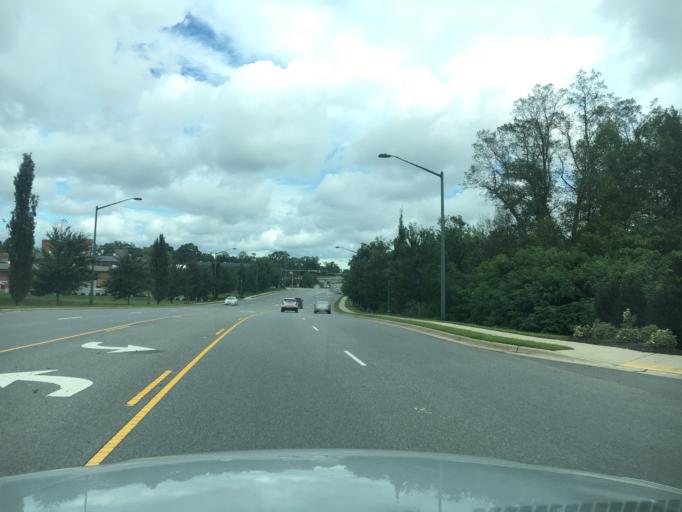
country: US
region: North Carolina
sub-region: Catawba County
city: Hickory
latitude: 35.7329
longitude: -81.3256
